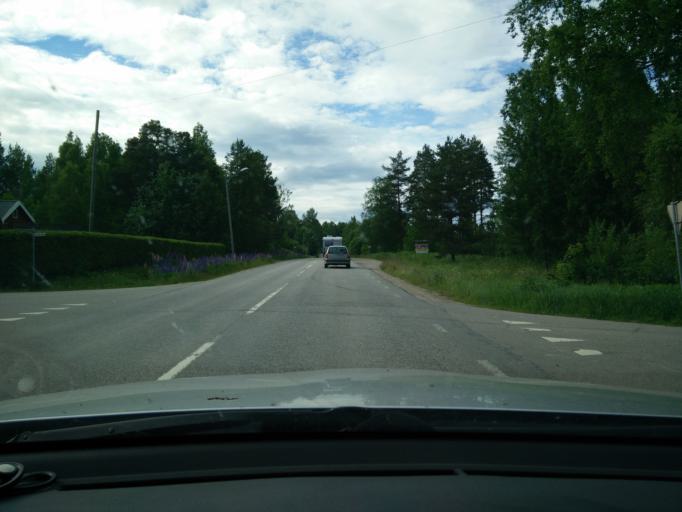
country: SE
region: Gaevleborg
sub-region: Nordanstigs Kommun
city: Bergsjoe
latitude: 61.9701
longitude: 17.0571
